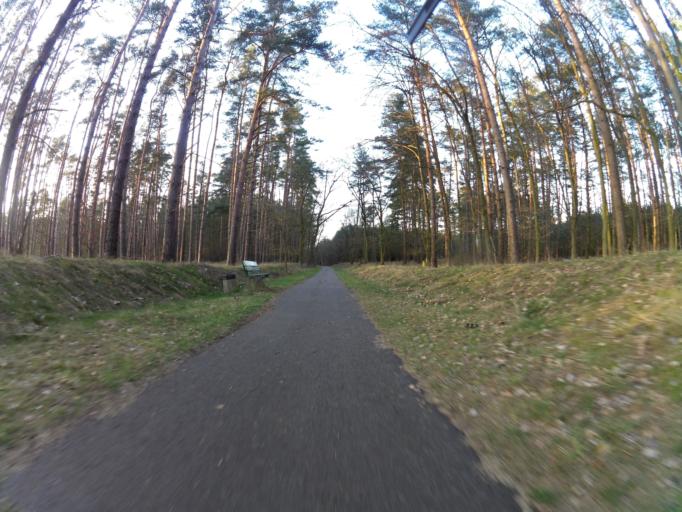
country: PL
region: West Pomeranian Voivodeship
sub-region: Powiat policki
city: Nowe Warpno
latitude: 53.7132
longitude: 14.3142
